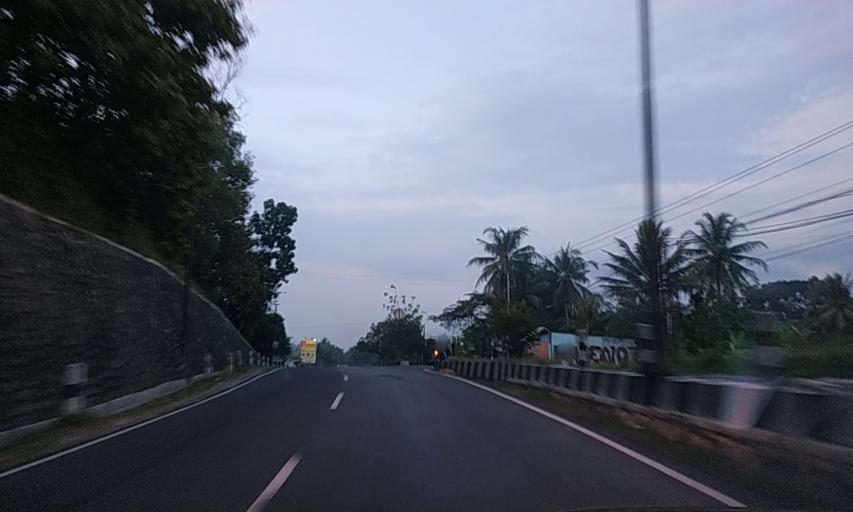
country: ID
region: Daerah Istimewa Yogyakarta
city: Srandakan
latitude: -7.8501
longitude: 110.2172
